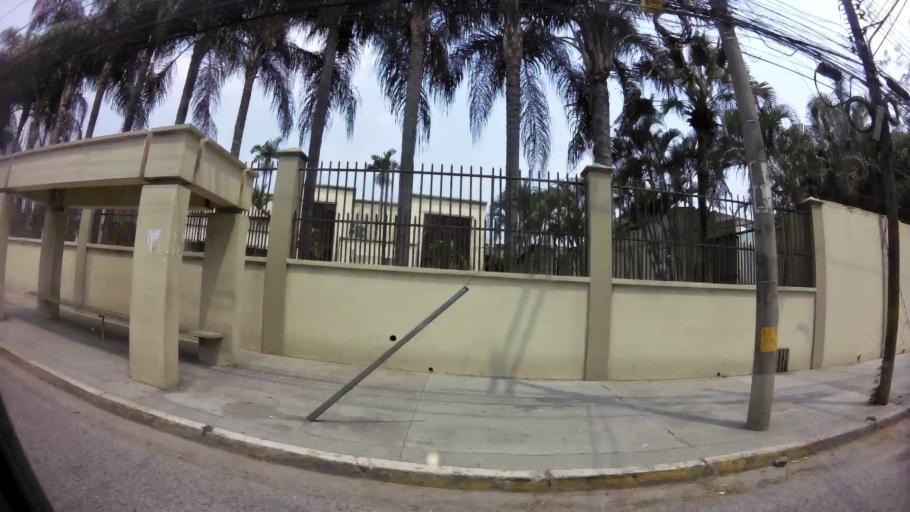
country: HN
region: Cortes
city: San Pedro Sula
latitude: 15.4890
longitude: -88.0271
